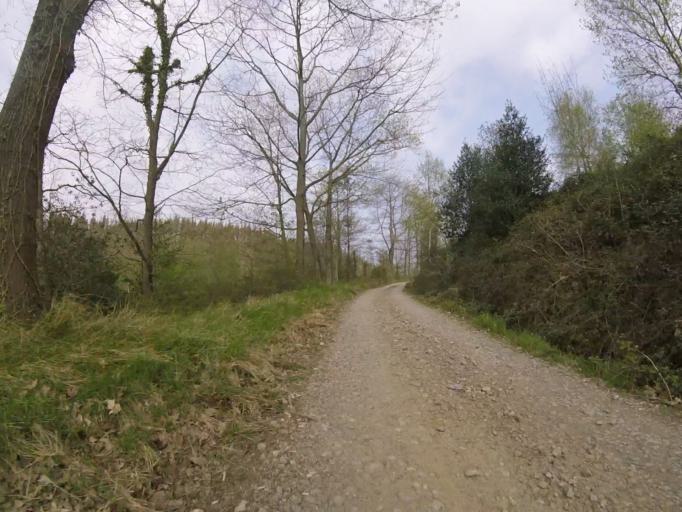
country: ES
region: Basque Country
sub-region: Provincia de Guipuzcoa
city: Usurbil
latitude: 43.2476
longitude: -2.0844
